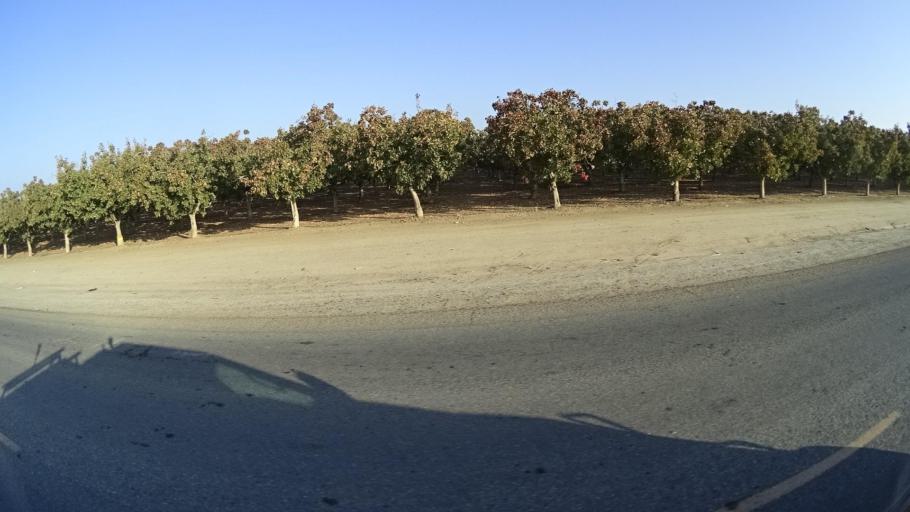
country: US
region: California
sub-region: Tulare County
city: Richgrove
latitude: 35.7906
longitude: -119.1633
